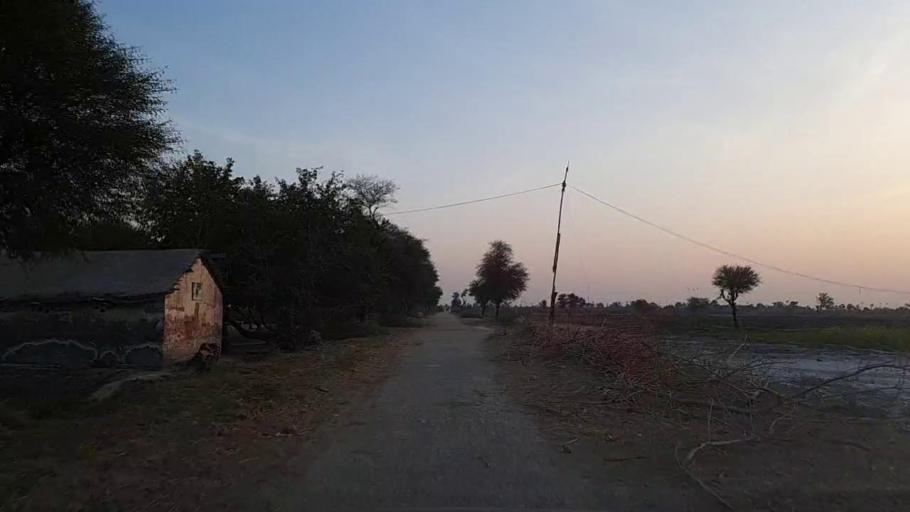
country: PK
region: Sindh
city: Tando Mittha Khan
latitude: 25.9519
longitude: 69.1164
